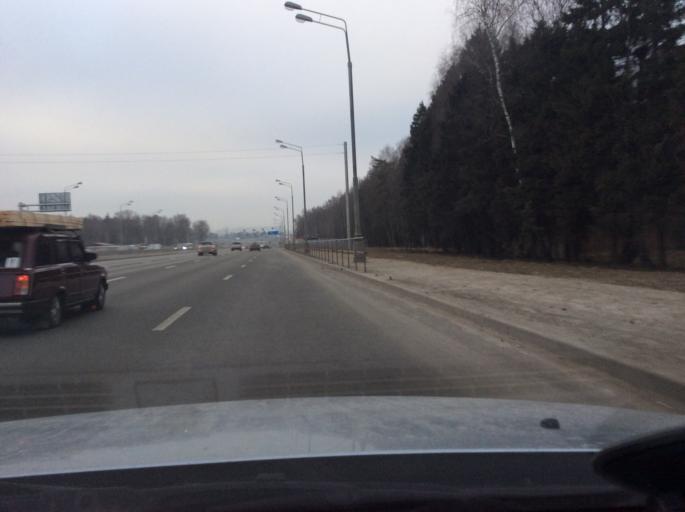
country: RU
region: Moskovskaya
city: Filimonki
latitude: 55.5435
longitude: 37.4085
